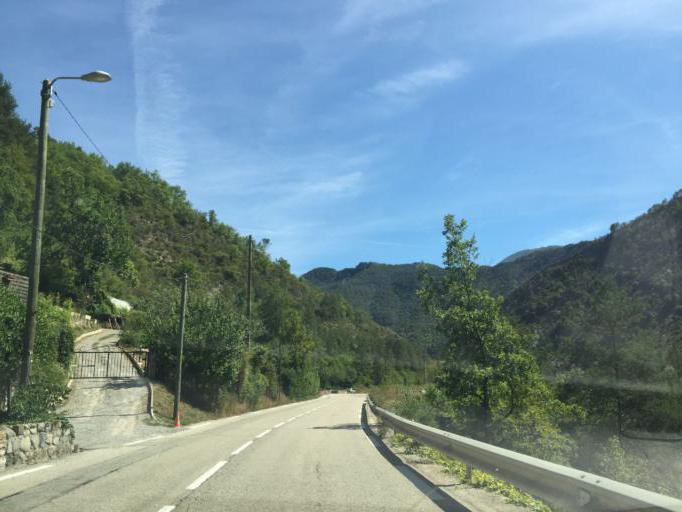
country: FR
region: Provence-Alpes-Cote d'Azur
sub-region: Departement des Alpes-Maritimes
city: Gilette
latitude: 43.9514
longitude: 7.1599
